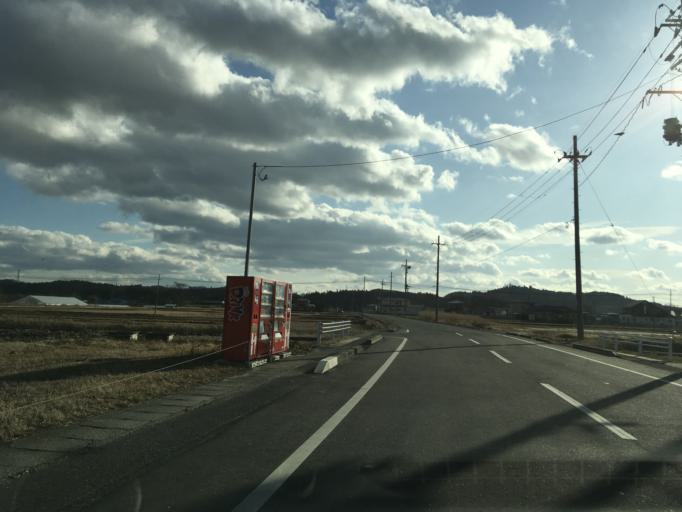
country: JP
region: Iwate
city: Ichinoseki
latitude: 38.8300
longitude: 140.9990
